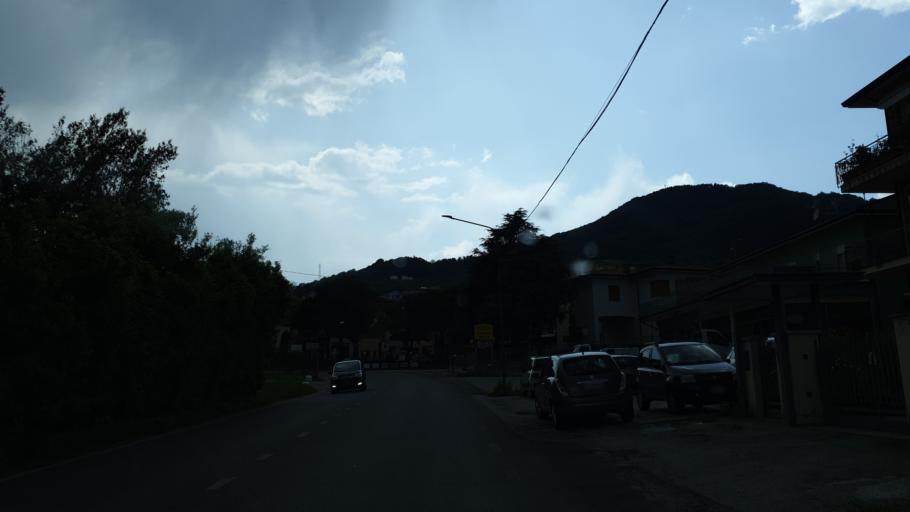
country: IT
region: Emilia-Romagna
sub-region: Provincia di Rimini
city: Novafeltria
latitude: 43.9002
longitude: 12.2922
